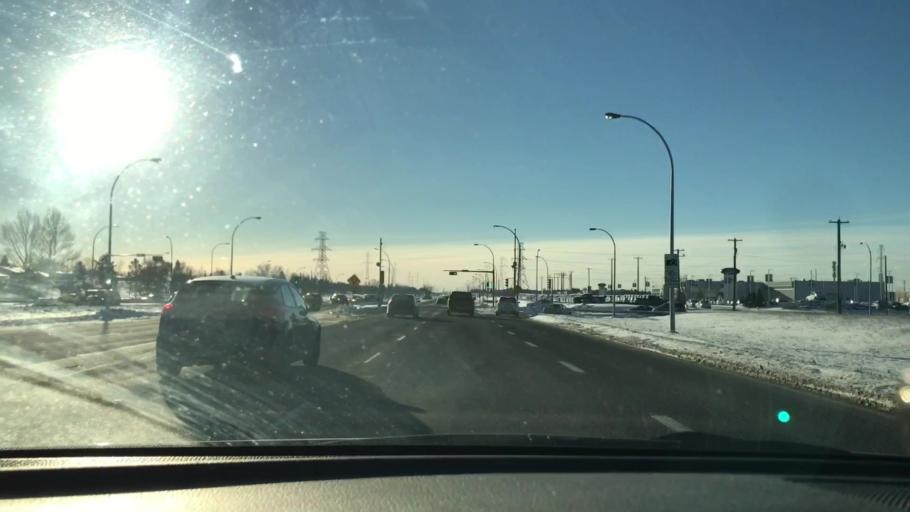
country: CA
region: Alberta
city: Edmonton
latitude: 53.4664
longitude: -113.4669
